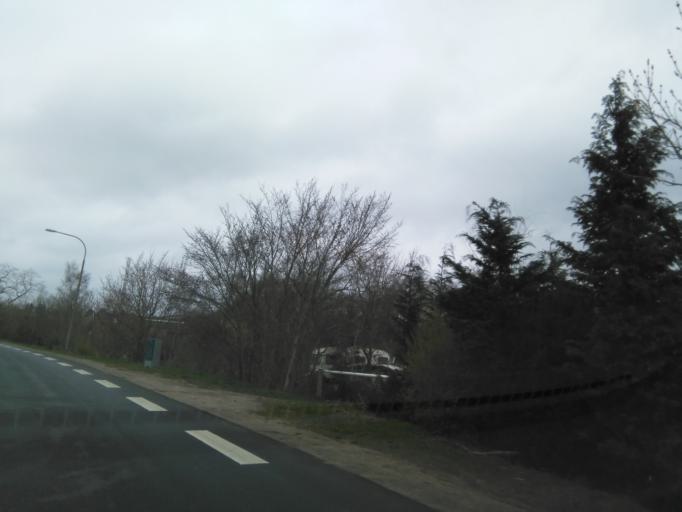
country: DK
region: Central Jutland
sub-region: Arhus Kommune
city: Stavtrup
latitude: 56.1617
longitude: 10.1025
